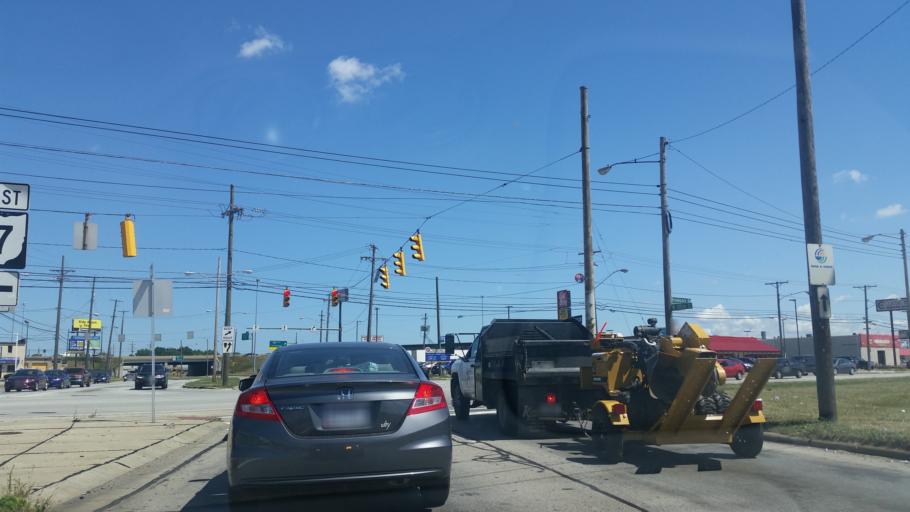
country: US
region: Ohio
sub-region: Cuyahoga County
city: Brook Park
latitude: 41.4181
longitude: -81.7812
